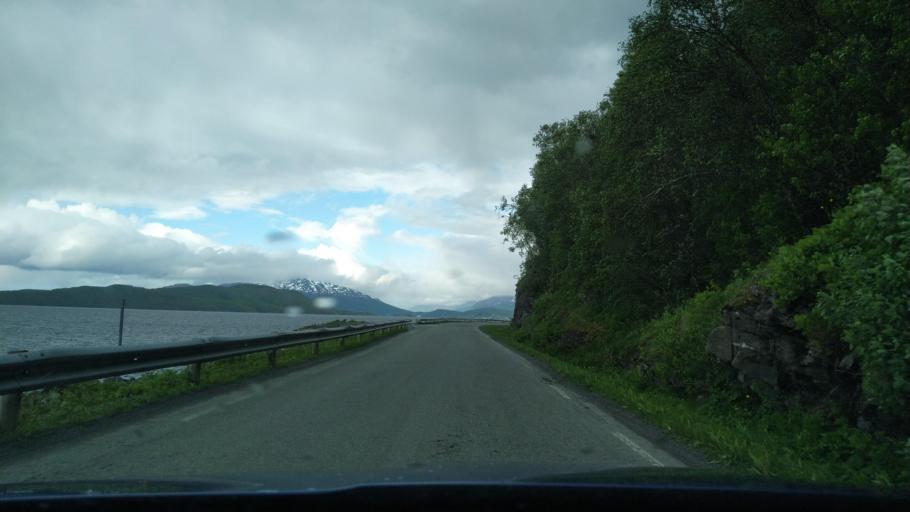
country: NO
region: Troms
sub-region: Lenvik
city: Finnsnes
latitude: 69.1436
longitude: 17.9217
